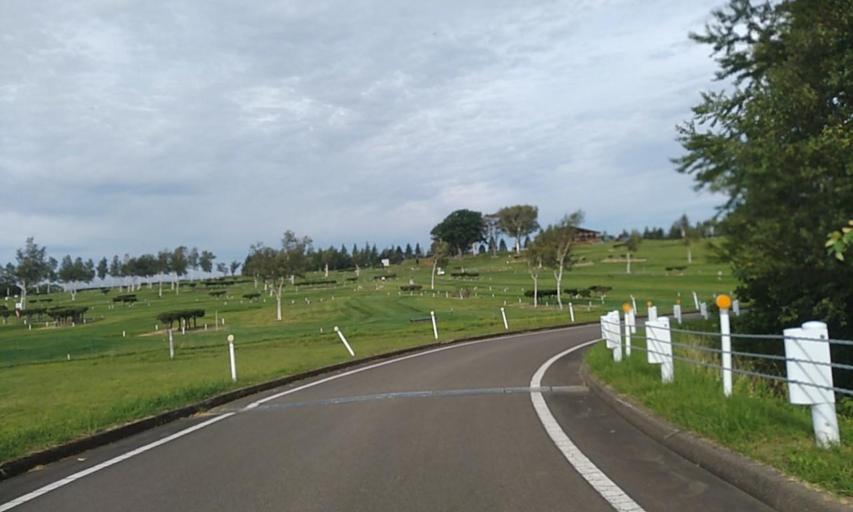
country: JP
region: Hokkaido
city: Abashiri
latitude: 43.7950
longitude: 144.5748
